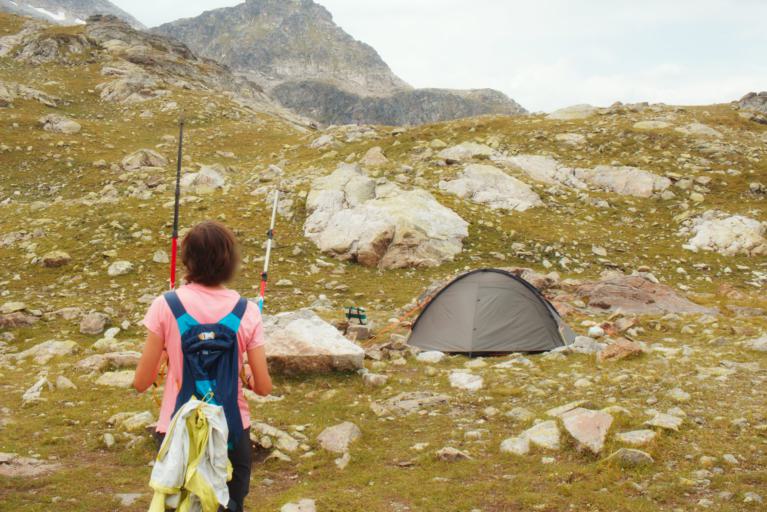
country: RU
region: Karachayevo-Cherkesiya
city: Nizhniy Arkhyz
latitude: 43.4512
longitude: 41.2346
